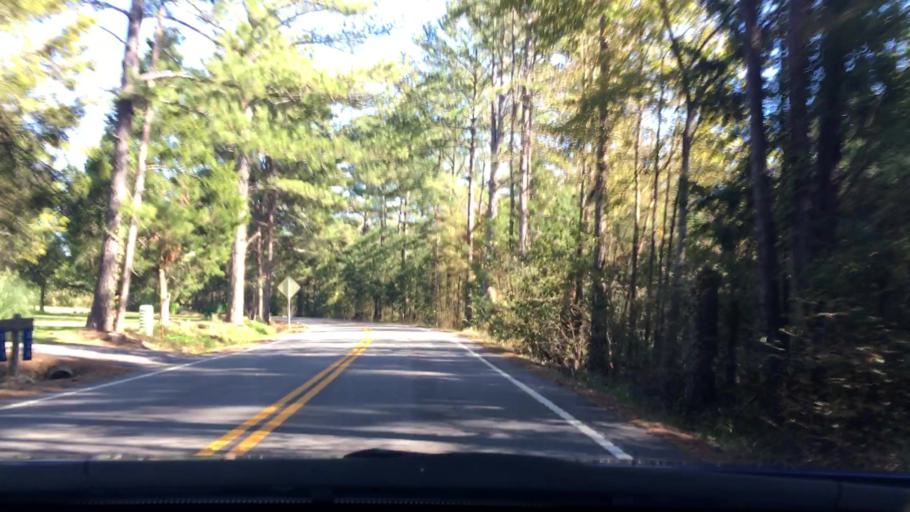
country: US
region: South Carolina
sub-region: Lexington County
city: Irmo
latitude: 34.1113
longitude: -81.1713
